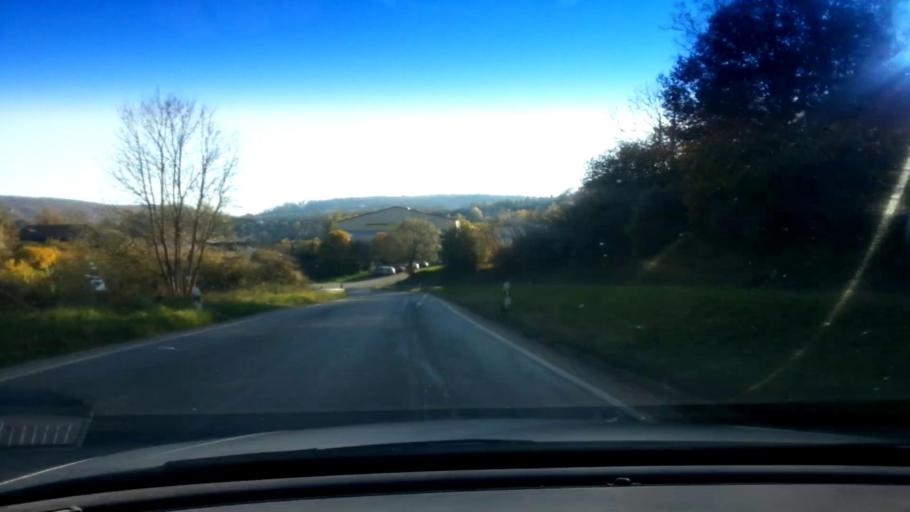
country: DE
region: Bavaria
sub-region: Upper Franconia
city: Poxdorf
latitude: 49.8879
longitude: 11.1280
